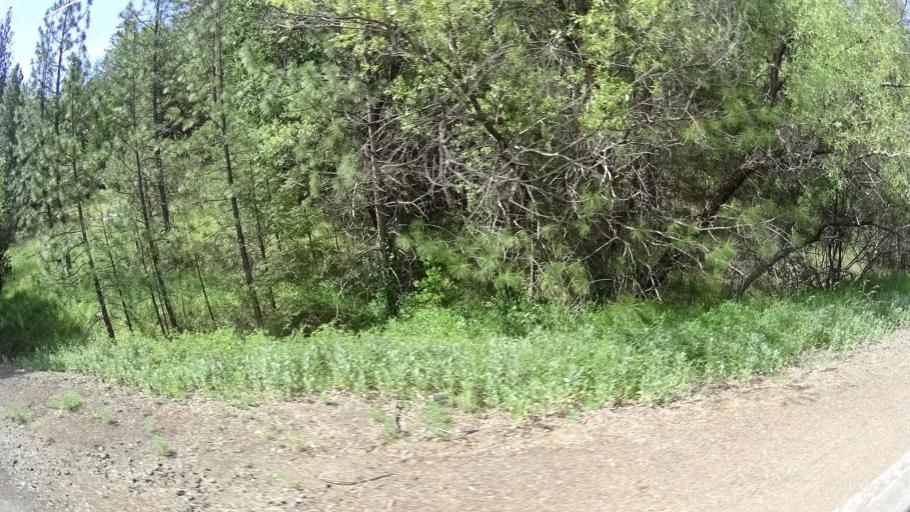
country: US
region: California
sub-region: Lake County
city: Cobb
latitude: 38.8554
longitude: -122.7347
